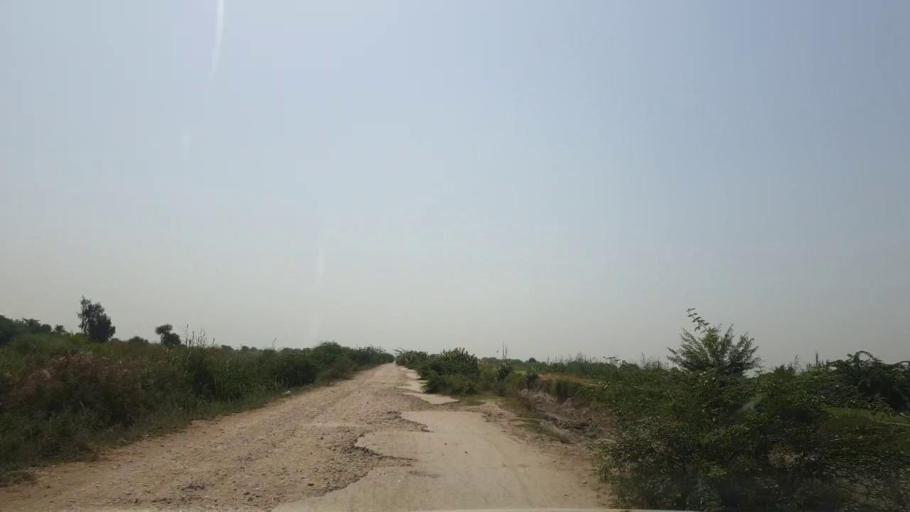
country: PK
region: Sindh
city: Jhol
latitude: 25.8803
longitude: 69.0370
